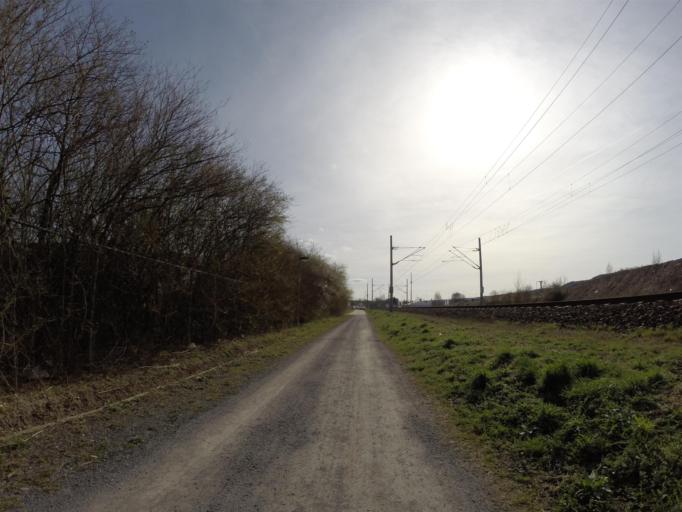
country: DE
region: Thuringia
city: Neuengonna
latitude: 50.9577
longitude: 11.6231
